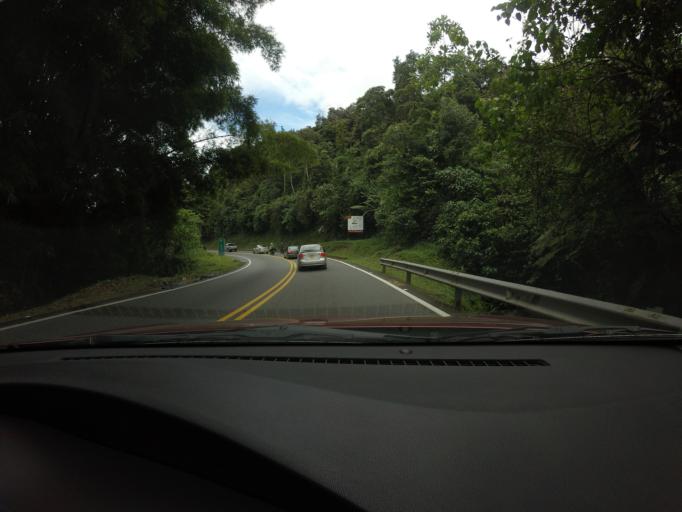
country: CO
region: Antioquia
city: Cocorna
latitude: 6.0341
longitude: -75.1929
